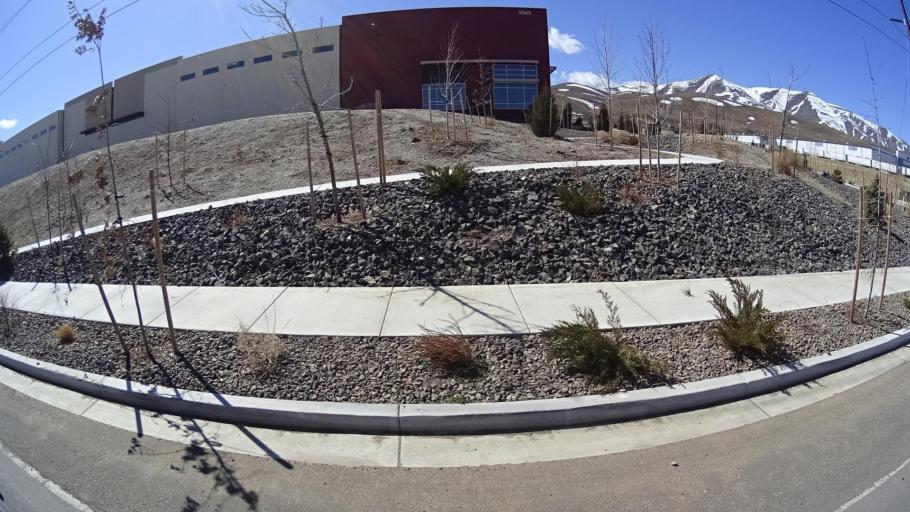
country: US
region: Nevada
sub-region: Washoe County
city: Lemmon Valley
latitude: 39.6054
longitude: -119.8762
